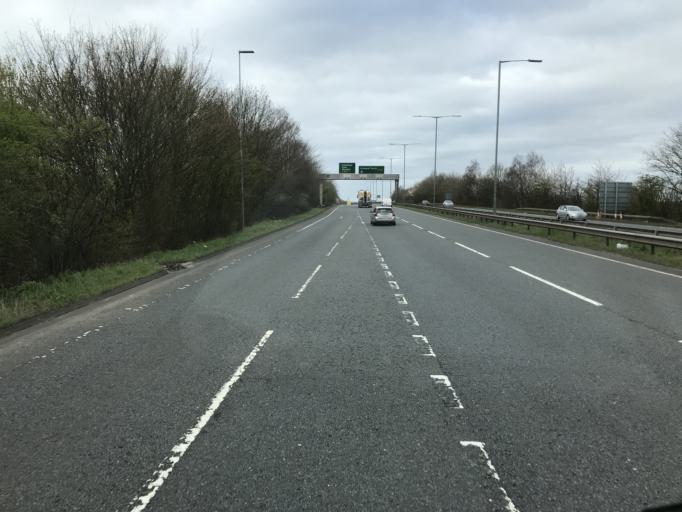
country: GB
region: England
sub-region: Borough of Halton
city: Hale
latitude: 53.3590
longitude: -2.7936
